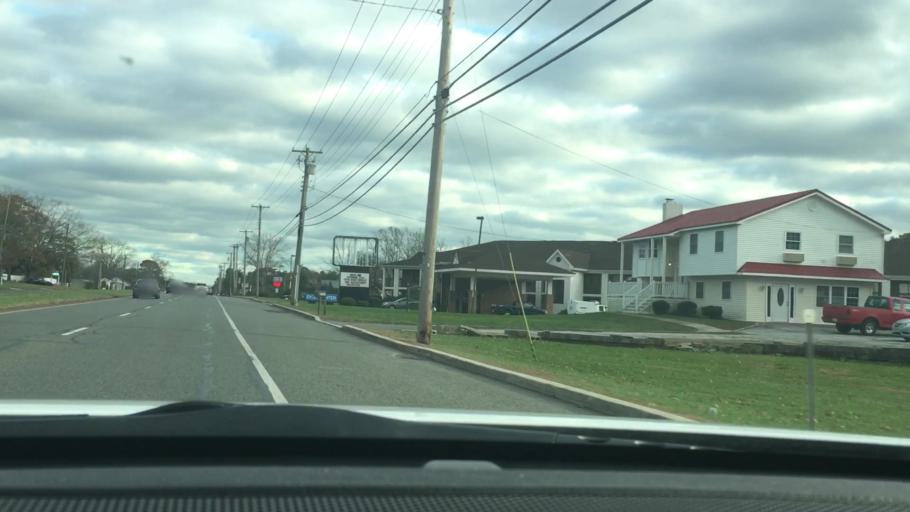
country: US
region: New Jersey
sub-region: Atlantic County
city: Northfield
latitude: 39.4143
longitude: -74.5757
